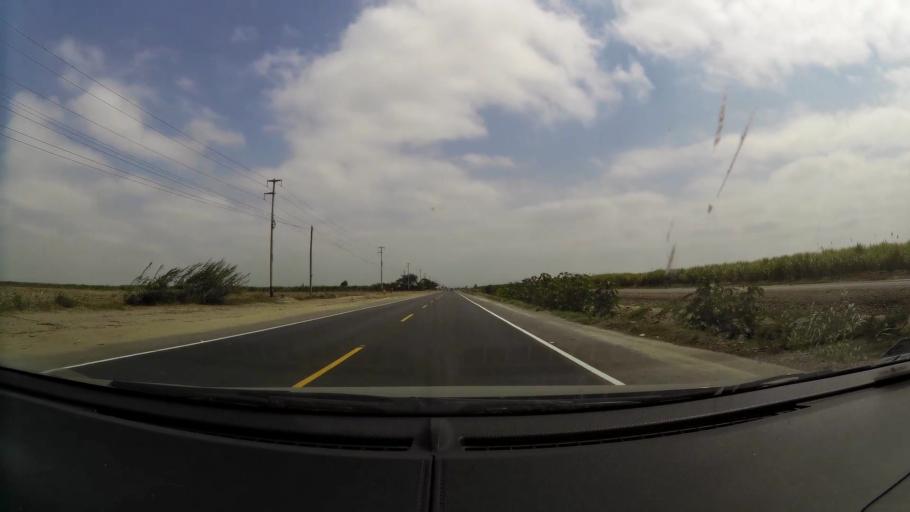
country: PE
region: La Libertad
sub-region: Ascope
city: Chicama
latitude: -7.8306
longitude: -79.1617
